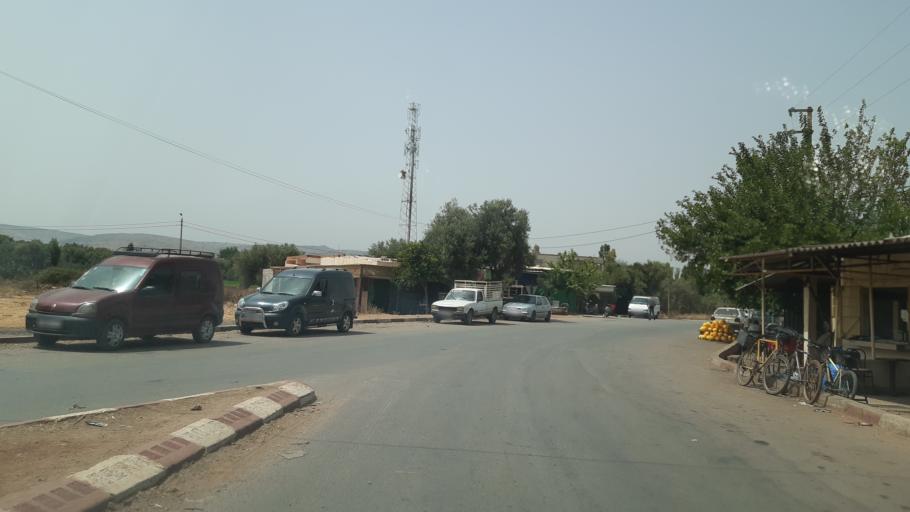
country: MA
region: Fes-Boulemane
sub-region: Fes
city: Oulad Tayeb
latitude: 33.8309
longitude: -5.1519
